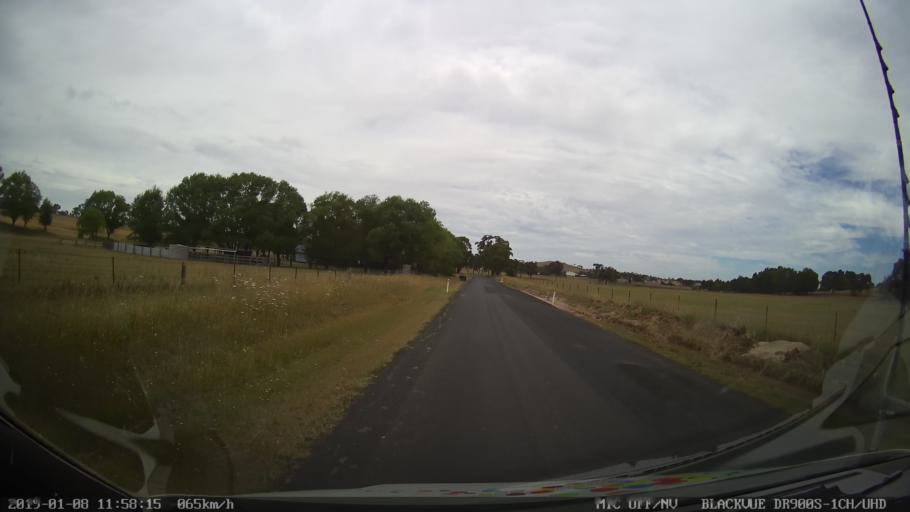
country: AU
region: New South Wales
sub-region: Armidale Dumaresq
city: Armidale
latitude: -30.4557
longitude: 151.5733
